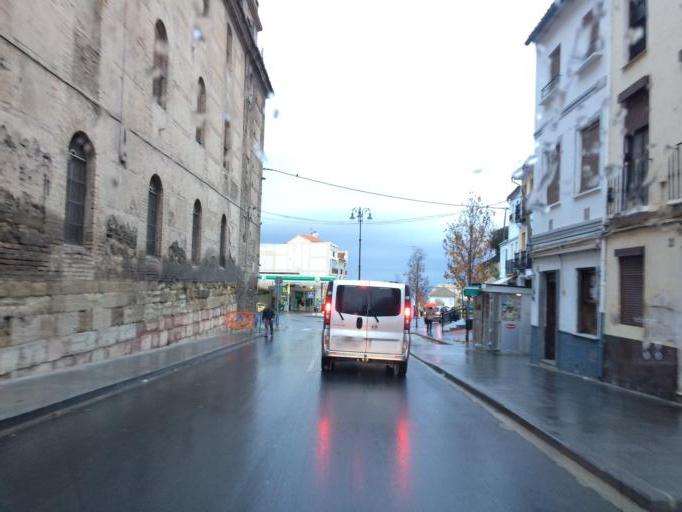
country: ES
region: Andalusia
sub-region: Provincia de Malaga
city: Antequera
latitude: 37.0226
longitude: -4.5595
